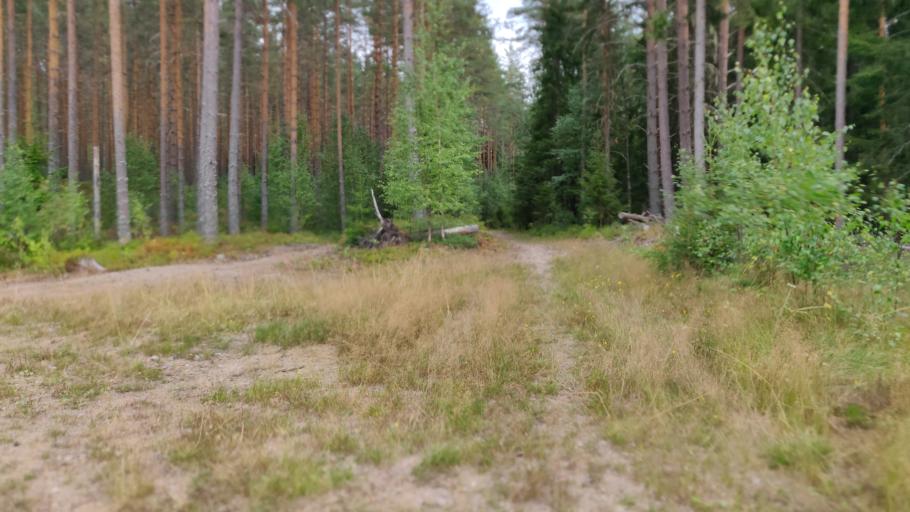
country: SE
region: Vaermland
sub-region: Hagfors Kommun
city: Hagfors
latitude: 60.0336
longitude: 13.5446
